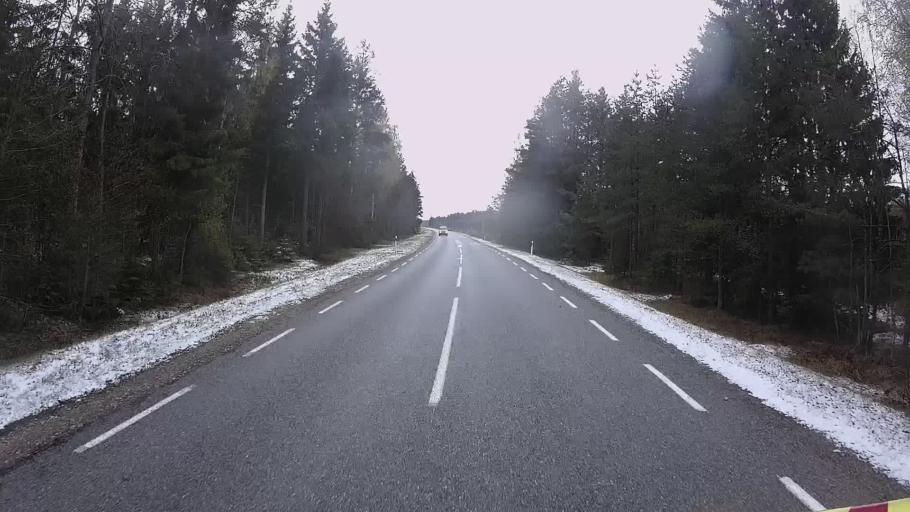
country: EE
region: Hiiumaa
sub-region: Kaerdla linn
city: Kardla
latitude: 59.0281
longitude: 22.6724
